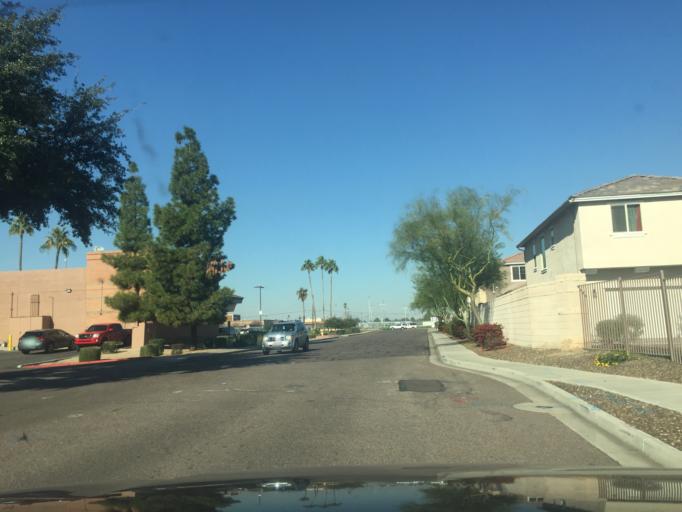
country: US
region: Arizona
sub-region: Maricopa County
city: Tolleson
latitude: 33.4787
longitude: -112.2171
